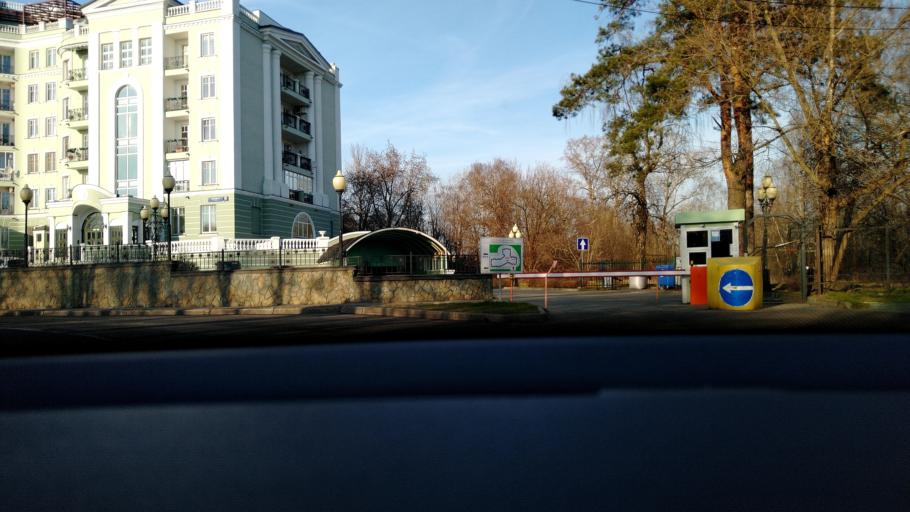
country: RU
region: Moskovskaya
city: Levoberezhnyy
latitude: 55.8306
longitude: 37.4706
